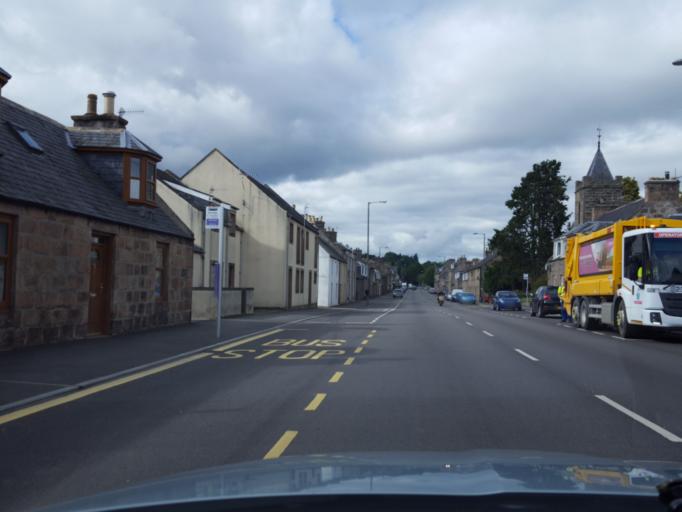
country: GB
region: Scotland
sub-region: Moray
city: Rothes
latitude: 57.4727
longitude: -3.2209
